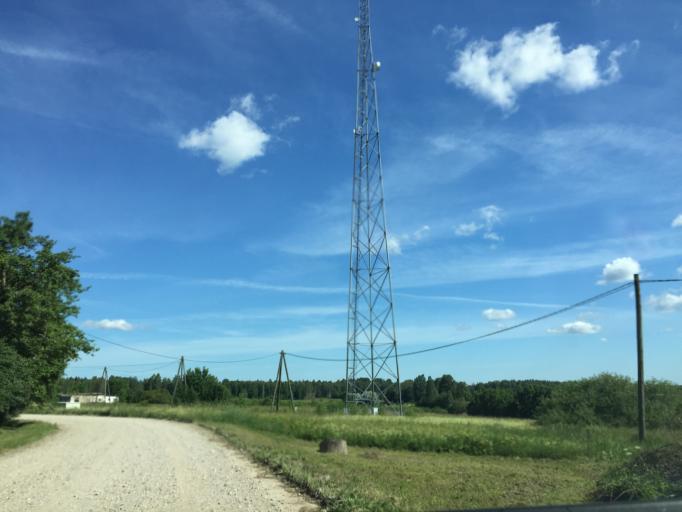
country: LV
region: Dundaga
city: Dundaga
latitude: 57.3598
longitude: 22.0308
